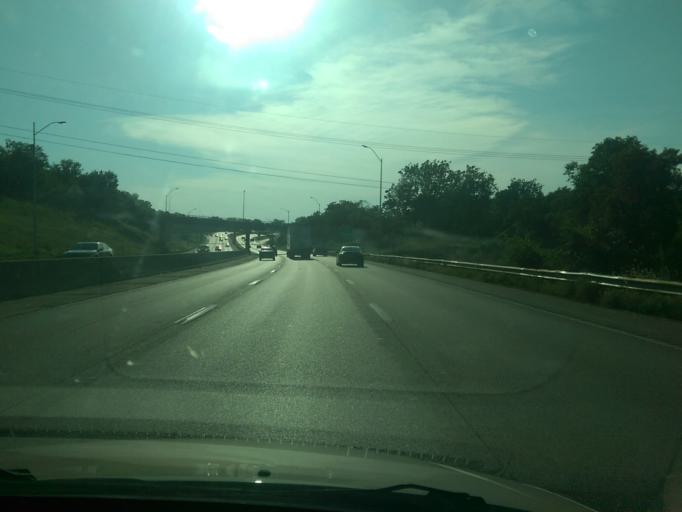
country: US
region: Missouri
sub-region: Jackson County
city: Kansas City
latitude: 39.0726
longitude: -94.5269
